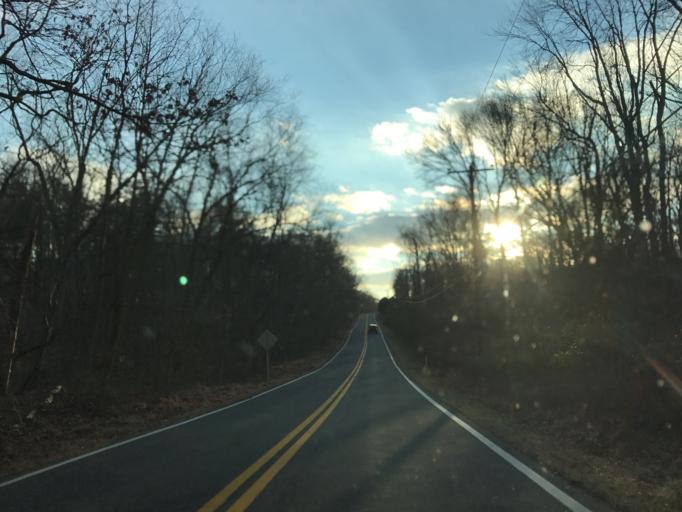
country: US
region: Maryland
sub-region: Cecil County
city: Charlestown
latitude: 39.4961
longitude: -75.9710
